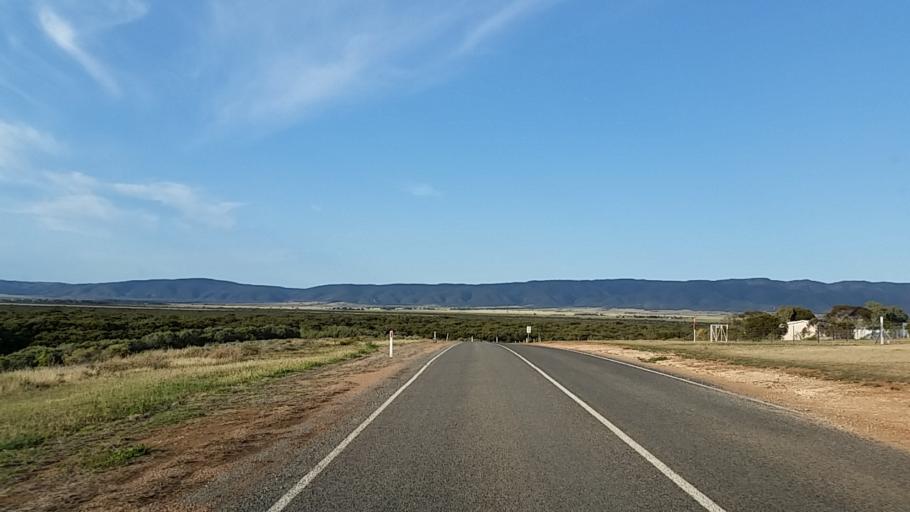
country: AU
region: South Australia
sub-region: Port Pirie City and Dists
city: Port Pirie
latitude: -33.0998
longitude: 138.0294
